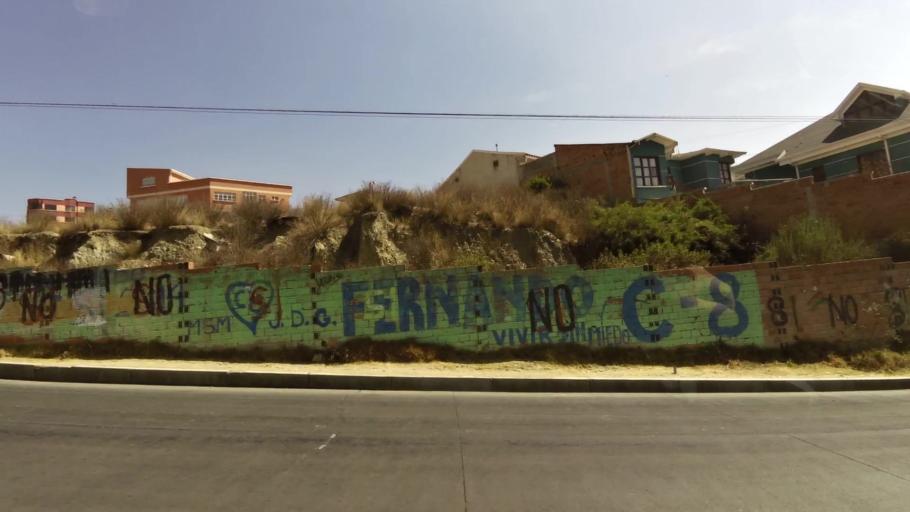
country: BO
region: La Paz
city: La Paz
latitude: -16.5327
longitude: -68.1306
